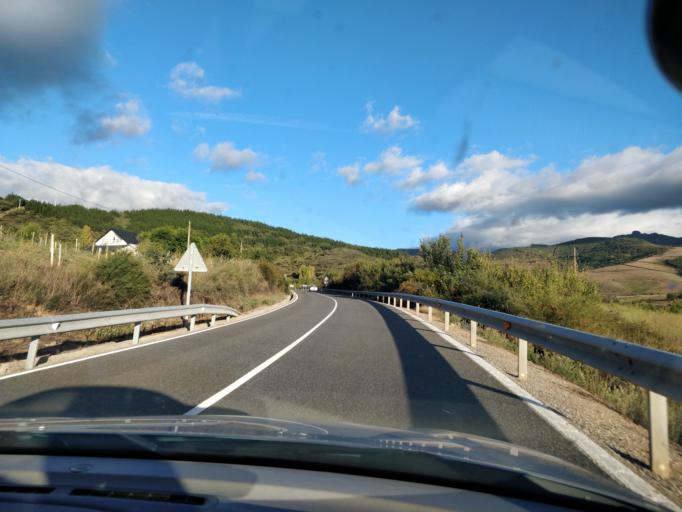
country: ES
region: Castille and Leon
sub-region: Provincia de Leon
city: Borrenes
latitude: 42.4983
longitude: -6.7235
